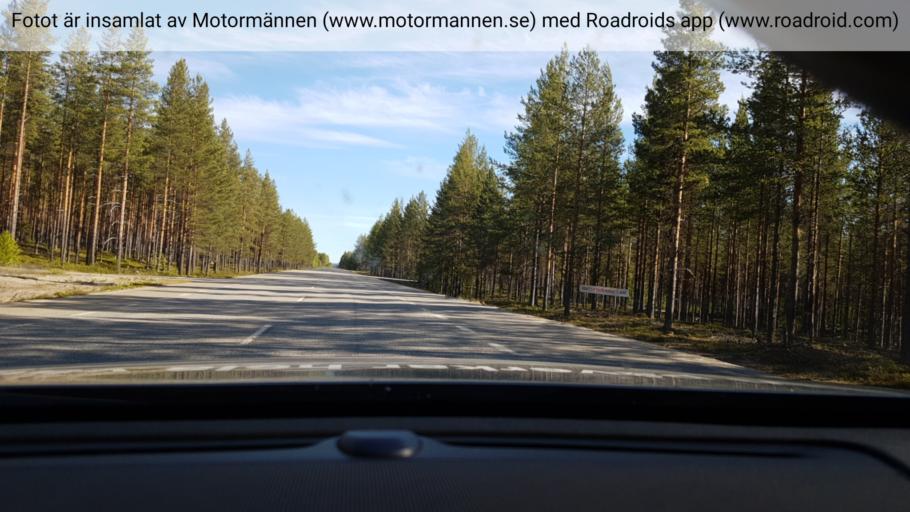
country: SE
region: Vaesterbotten
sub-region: Norsjo Kommun
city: Norsjoe
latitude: 64.5871
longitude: 19.2969
